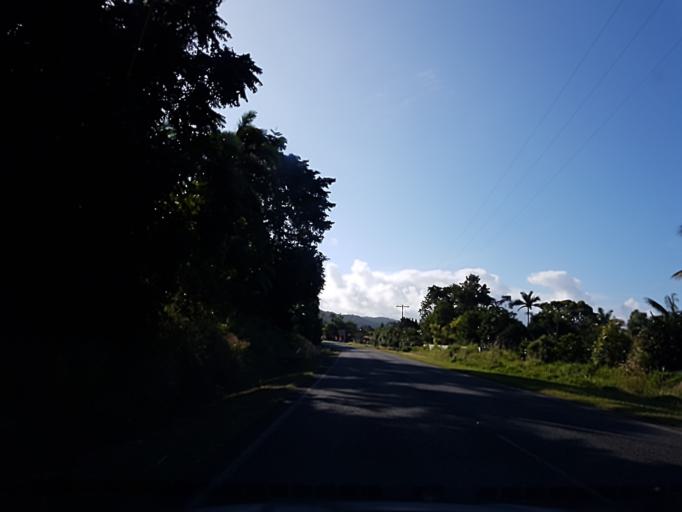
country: AU
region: Queensland
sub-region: Cairns
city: Port Douglas
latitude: -16.3617
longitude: 145.4116
